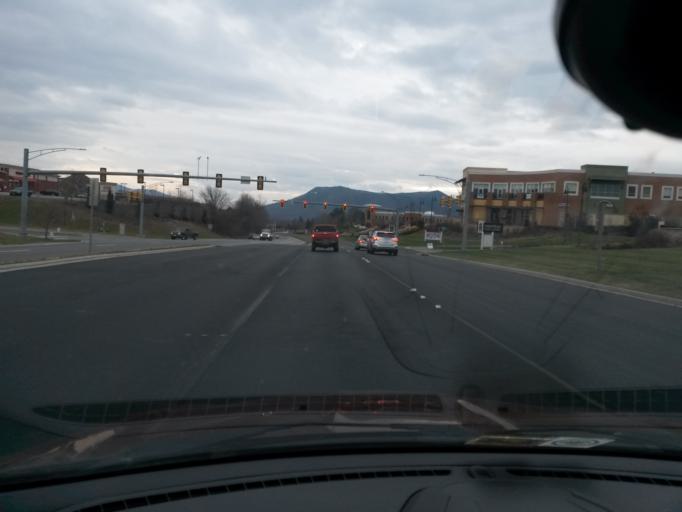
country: US
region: Virginia
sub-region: Botetourt County
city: Daleville
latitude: 37.4175
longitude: -79.9119
